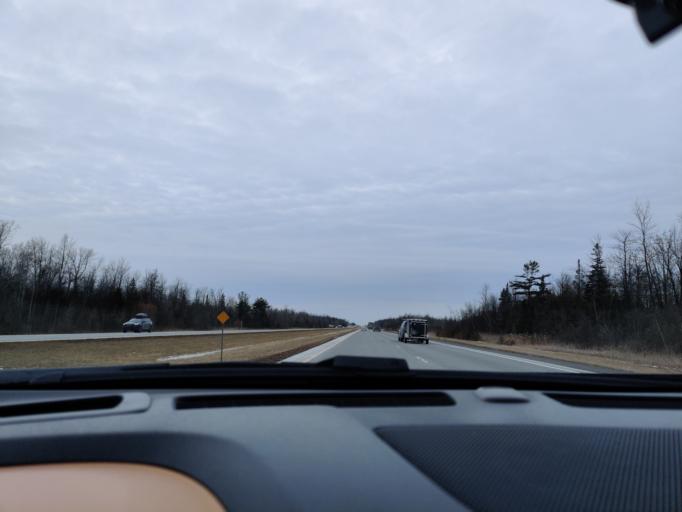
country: US
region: New York
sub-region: St. Lawrence County
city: Ogdensburg
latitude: 44.8477
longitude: -75.3464
